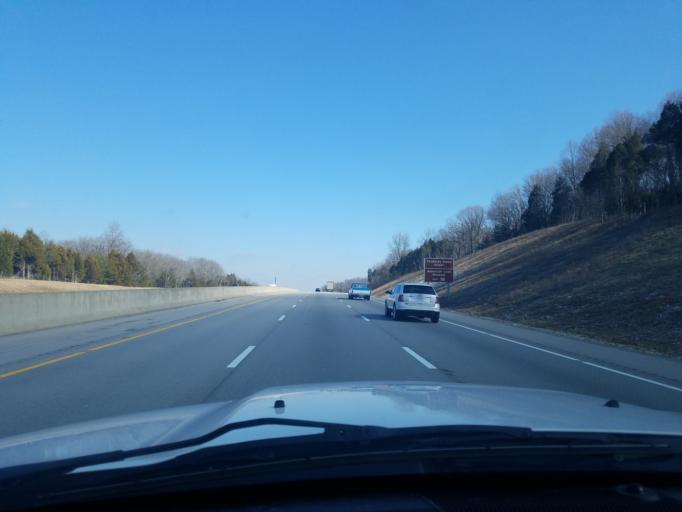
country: US
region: Kentucky
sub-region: Barren County
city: Cave City
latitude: 37.1734
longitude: -85.9563
